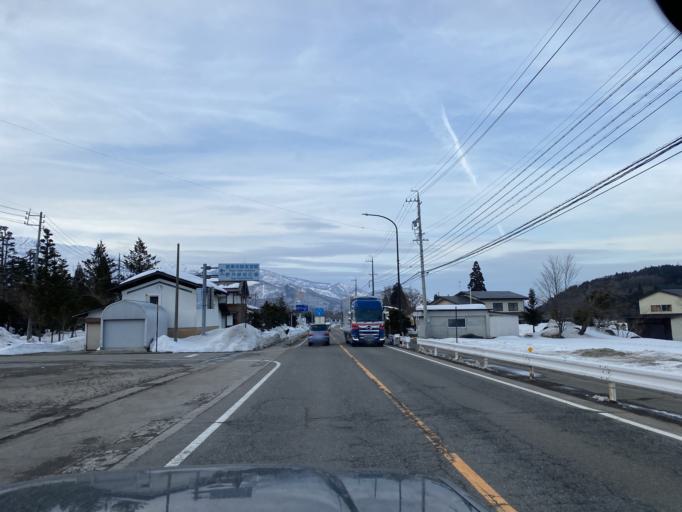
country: JP
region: Nagano
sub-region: Kitaazumi Gun
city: Hakuba
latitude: 36.6641
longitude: 137.8489
